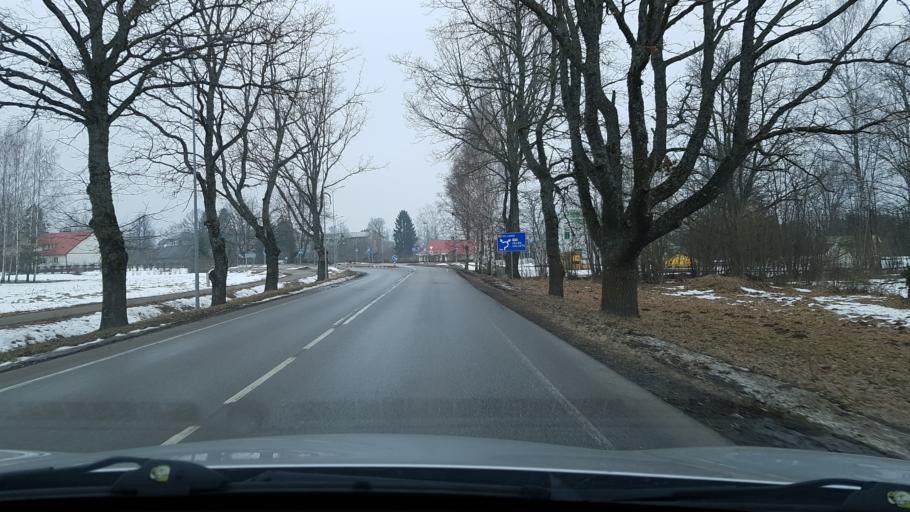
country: EE
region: Valgamaa
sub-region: Torva linn
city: Torva
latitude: 58.2325
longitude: 25.8813
